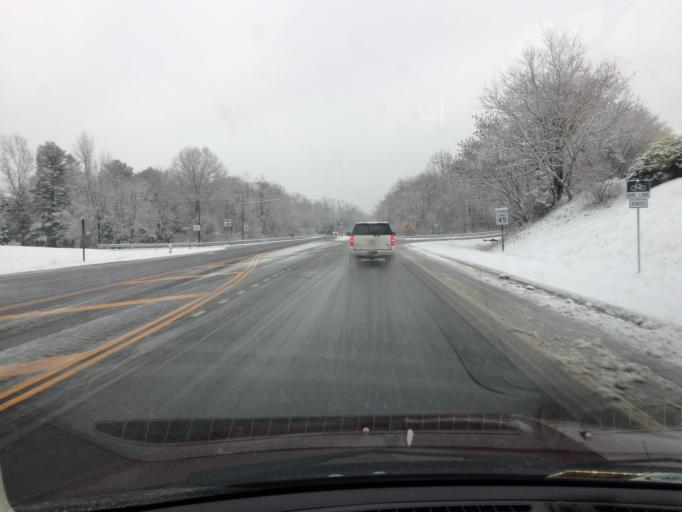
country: US
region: Virginia
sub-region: Amherst County
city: Amherst
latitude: 37.5848
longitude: -79.0477
